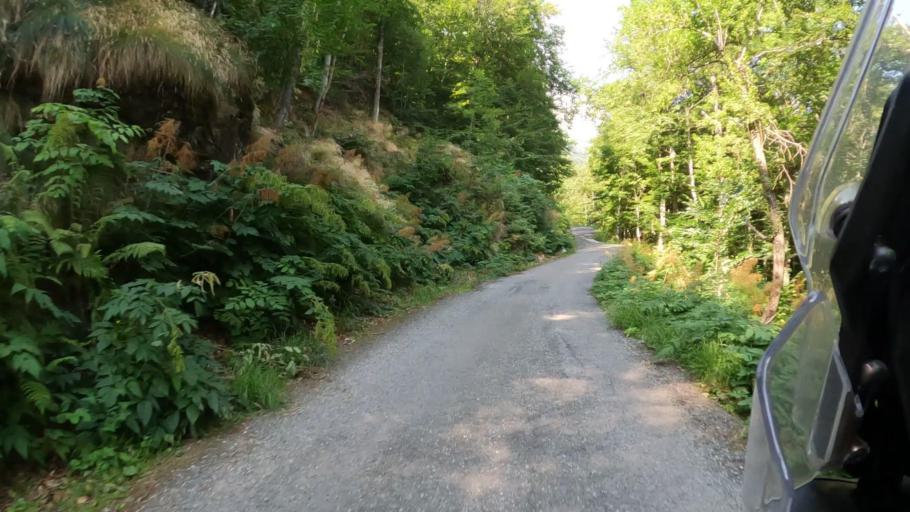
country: IT
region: Piedmont
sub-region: Provincia di Torino
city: Lemie
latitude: 45.2186
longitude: 7.3130
